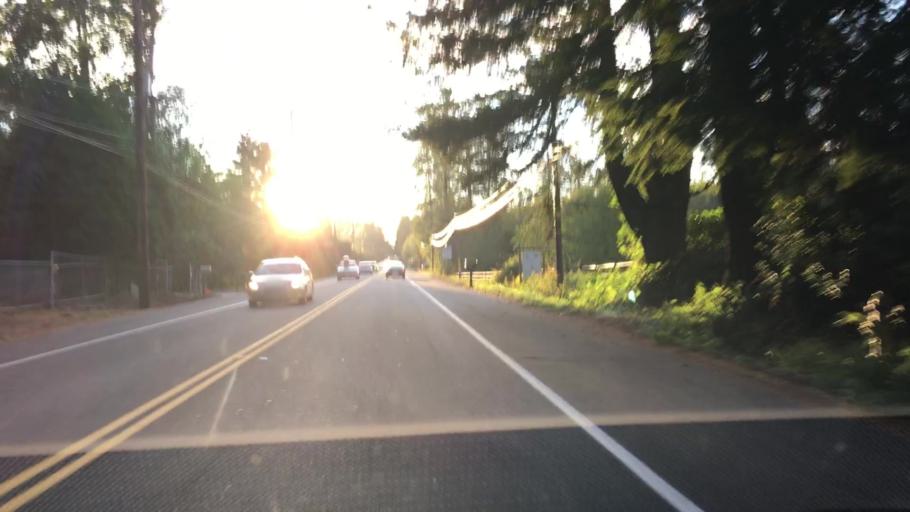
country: US
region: Washington
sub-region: King County
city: Cottage Lake
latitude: 47.7615
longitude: -122.1020
